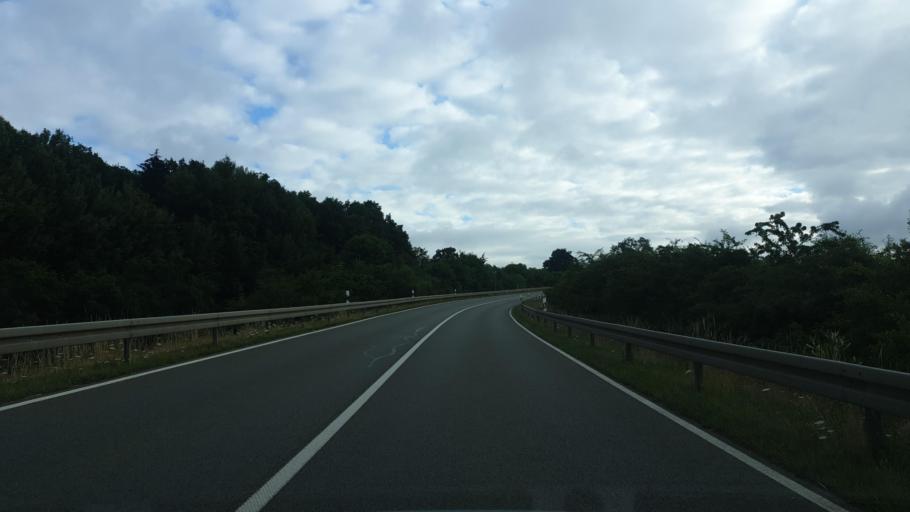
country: DE
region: Saxony
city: Limbach
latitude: 50.5733
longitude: 12.2189
